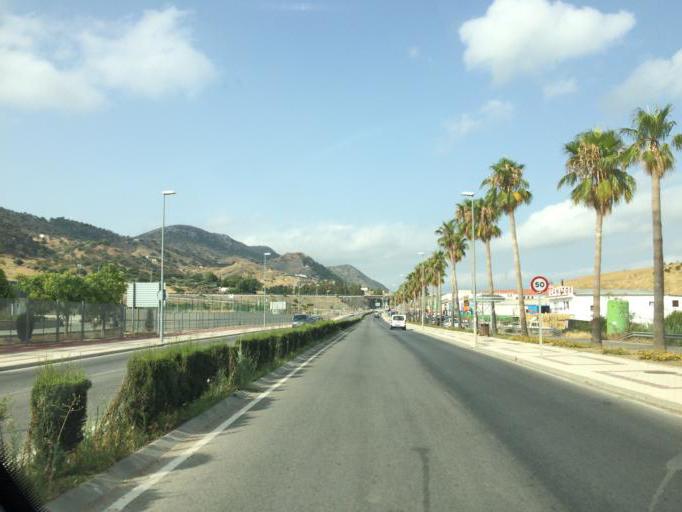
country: ES
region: Andalusia
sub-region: Provincia de Malaga
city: Estacion de Cartama
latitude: 36.7210
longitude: -4.6172
